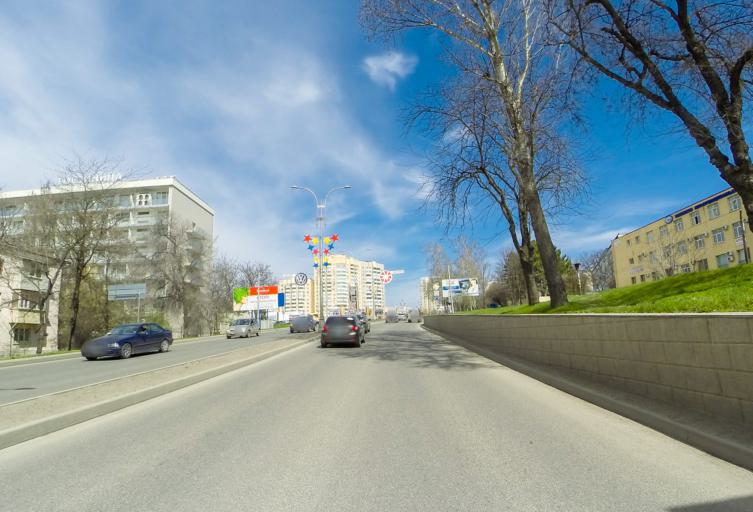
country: RU
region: Stavropol'skiy
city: Pyatigorsk
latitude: 44.0519
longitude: 43.0649
